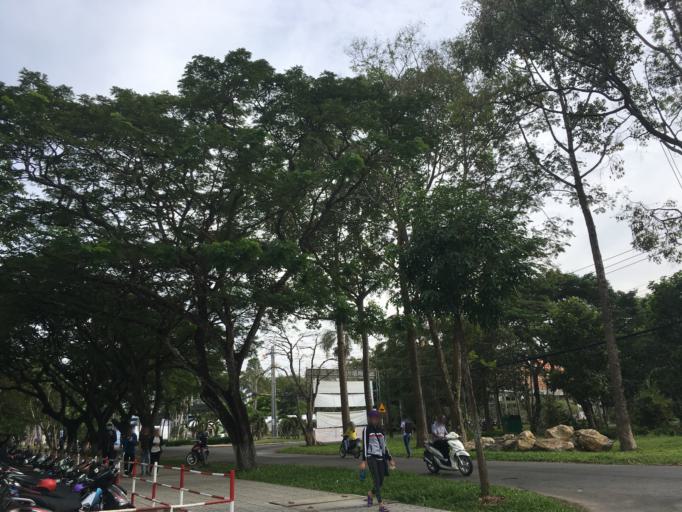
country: VN
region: Can Tho
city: Can Tho
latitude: 10.0304
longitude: 105.7690
